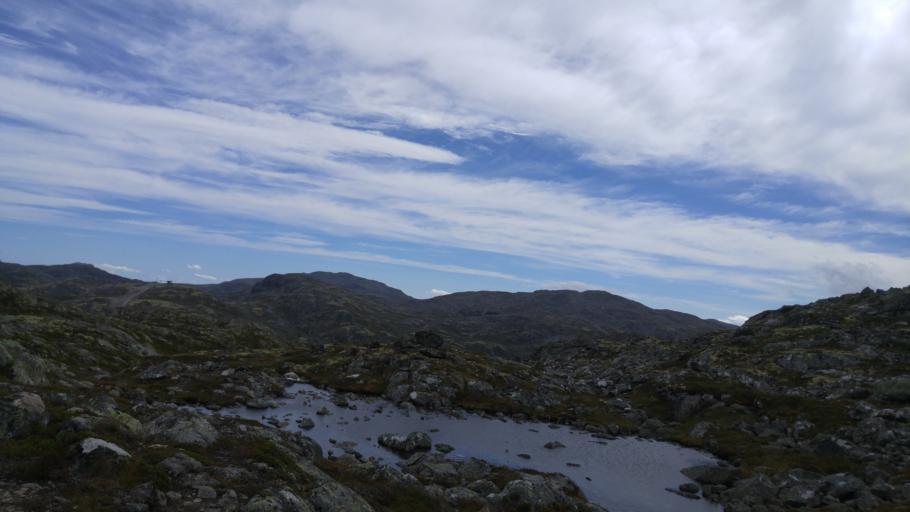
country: NO
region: Buskerud
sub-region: Hemsedal
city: Hemsedal
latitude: 60.8532
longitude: 8.4604
